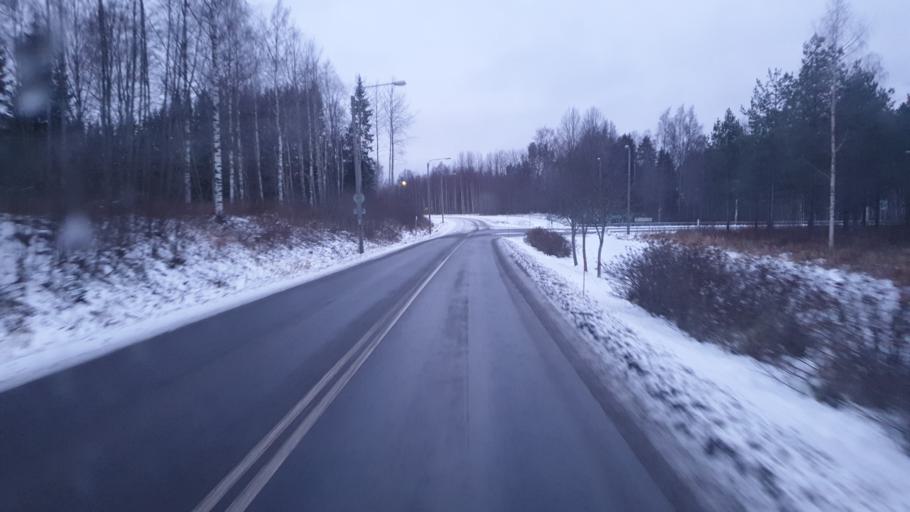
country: FI
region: Northern Savo
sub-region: Kuopio
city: Siilinjaervi
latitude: 63.0591
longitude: 27.6698
